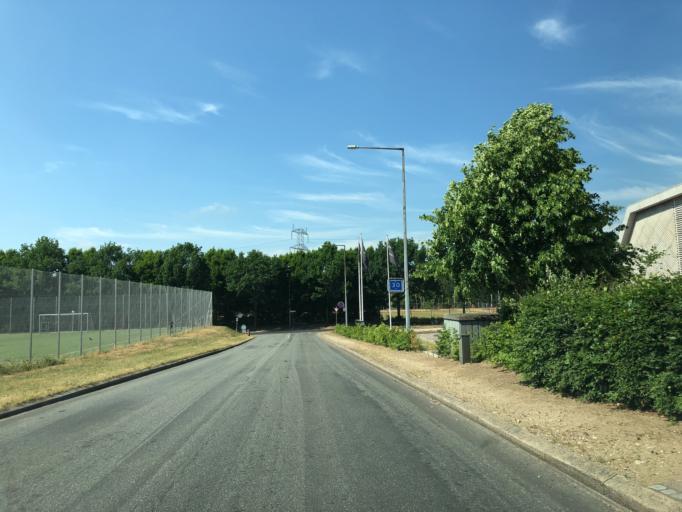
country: DK
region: South Denmark
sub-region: Kolding Kommune
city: Kolding
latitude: 55.5278
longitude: 9.4706
